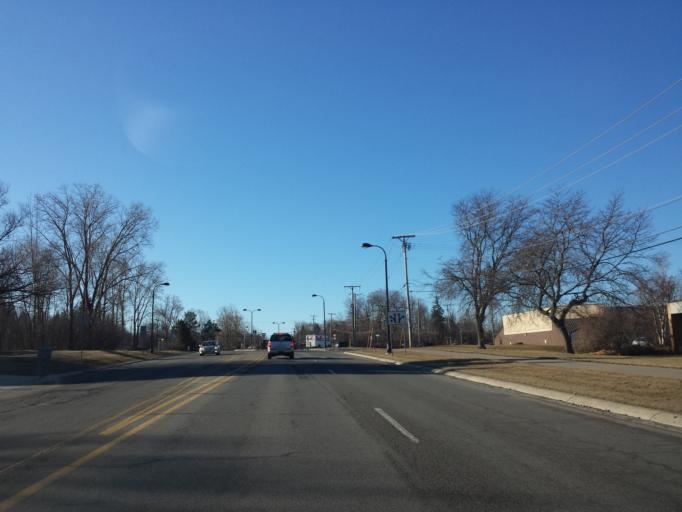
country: US
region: Michigan
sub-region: Oakland County
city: Rochester Hills
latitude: 42.6533
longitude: -83.1528
